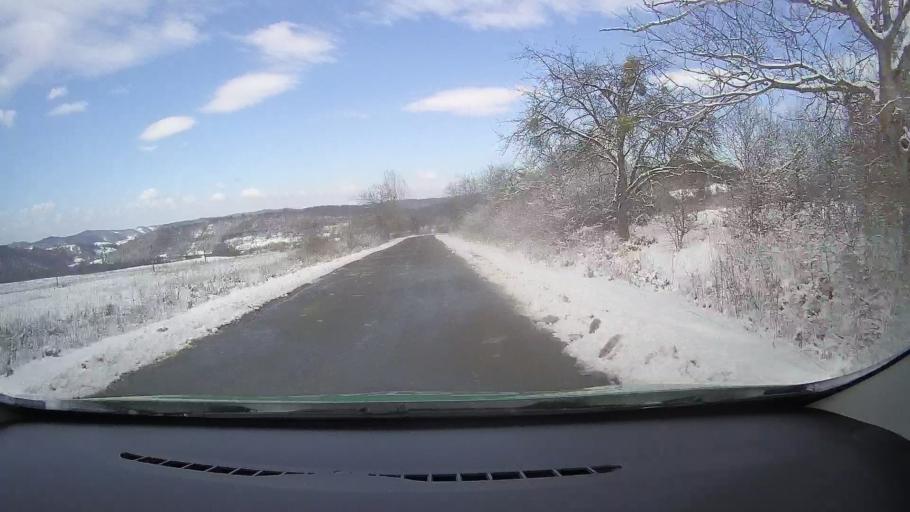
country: RO
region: Sibiu
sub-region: Comuna Mihaileni
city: Mihaileni
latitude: 46.0056
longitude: 24.4254
